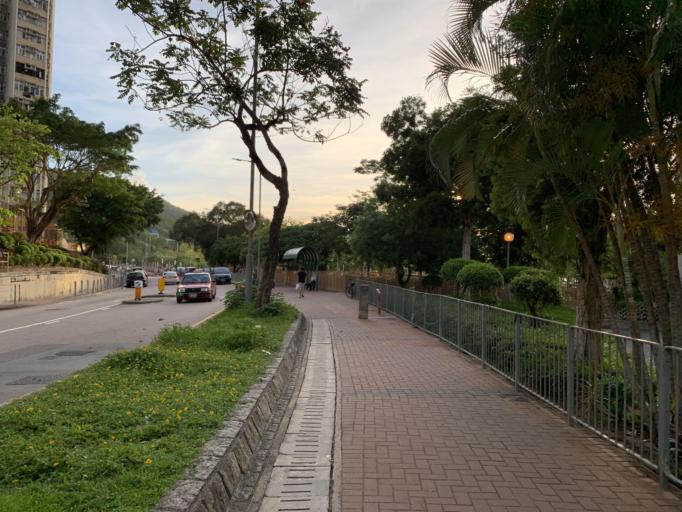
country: HK
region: Tsuen Wan
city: Tsuen Wan
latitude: 22.3624
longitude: 114.1010
